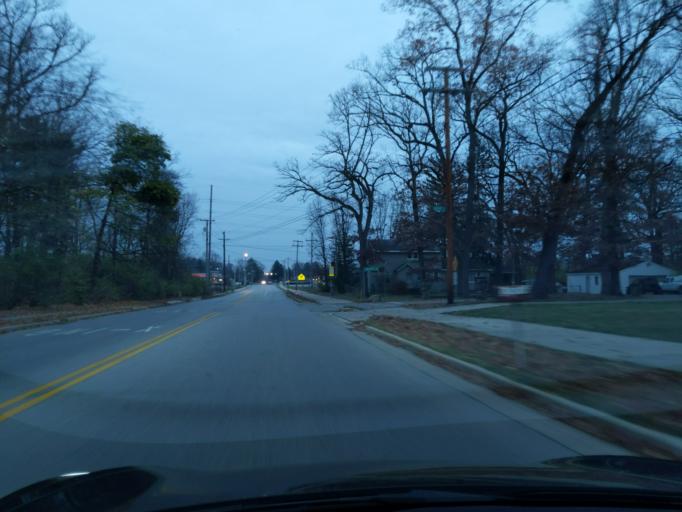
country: US
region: Indiana
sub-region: Saint Joseph County
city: Georgetown
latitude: 41.7304
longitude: -86.2544
